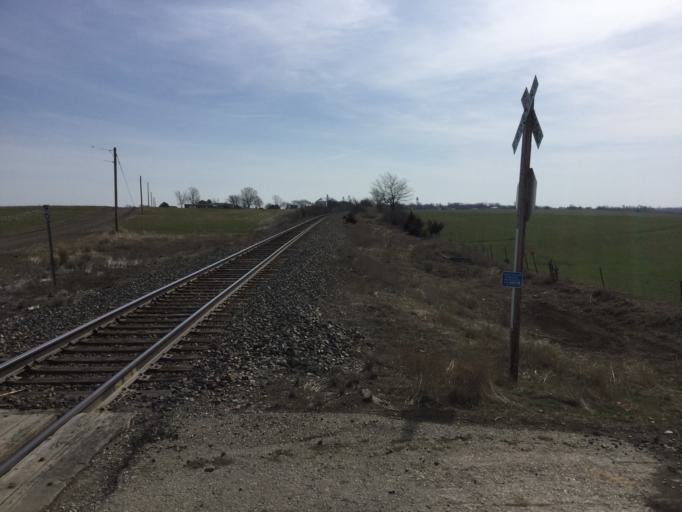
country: US
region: Kansas
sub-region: Nemaha County
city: Seneca
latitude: 39.8782
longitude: -96.2772
